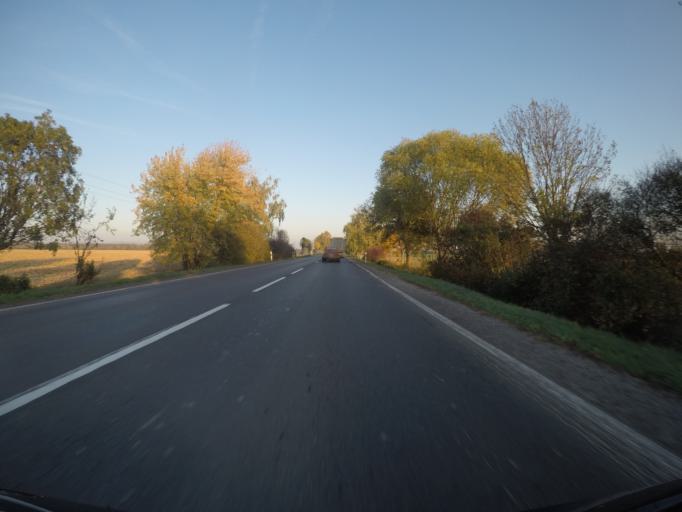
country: HU
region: Baranya
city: Szentlorinc
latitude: 46.0390
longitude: 17.9336
